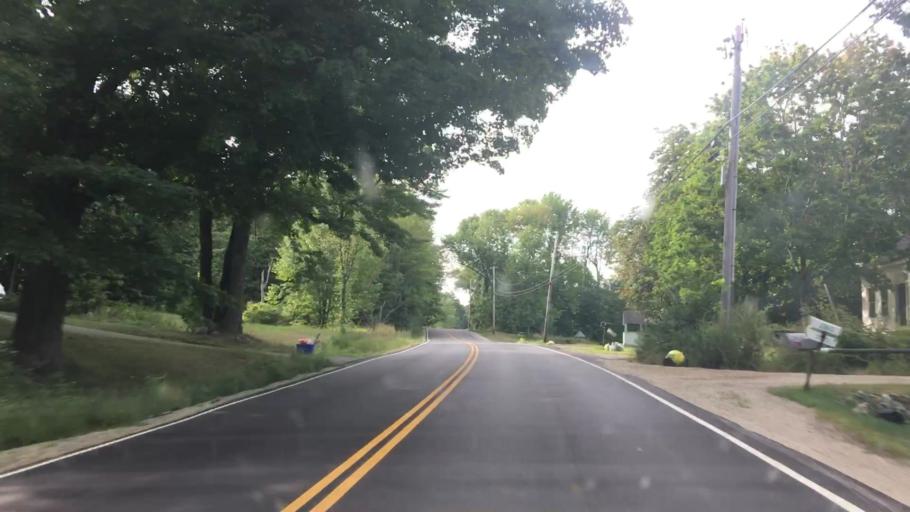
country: US
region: Maine
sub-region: Cumberland County
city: Cumberland Center
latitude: 43.7792
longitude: -70.3034
